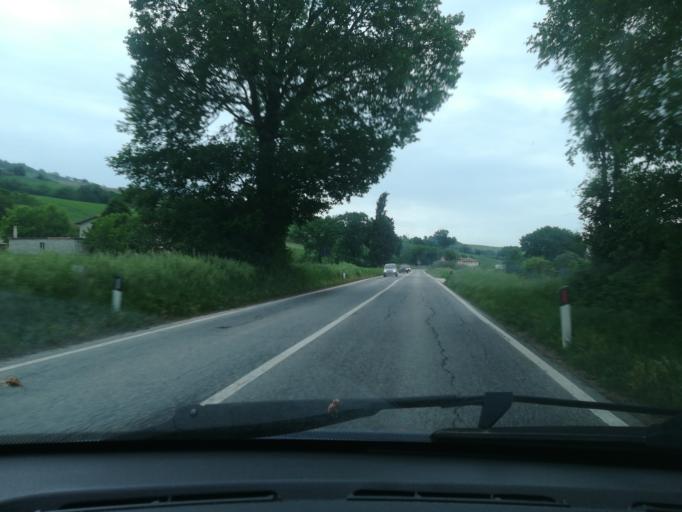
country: IT
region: The Marches
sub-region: Provincia di Macerata
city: Tolentino
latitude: 43.2629
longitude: 13.2428
